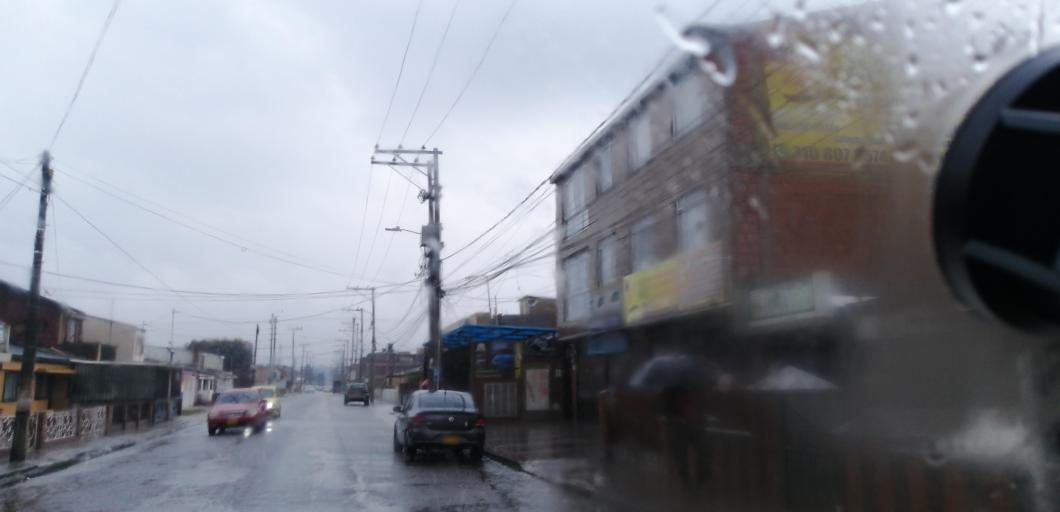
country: CO
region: Cundinamarca
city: Madrid
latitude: 4.7353
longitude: -74.2671
